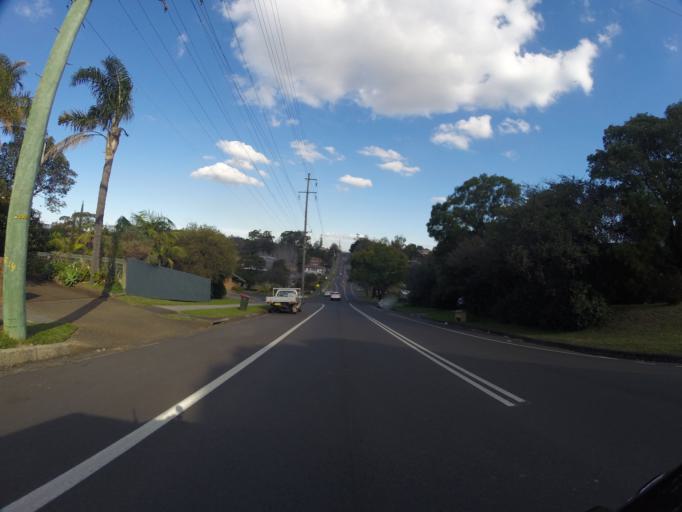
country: AU
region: New South Wales
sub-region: Wollongong
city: Keiraville
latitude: -34.4169
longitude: 150.8699
